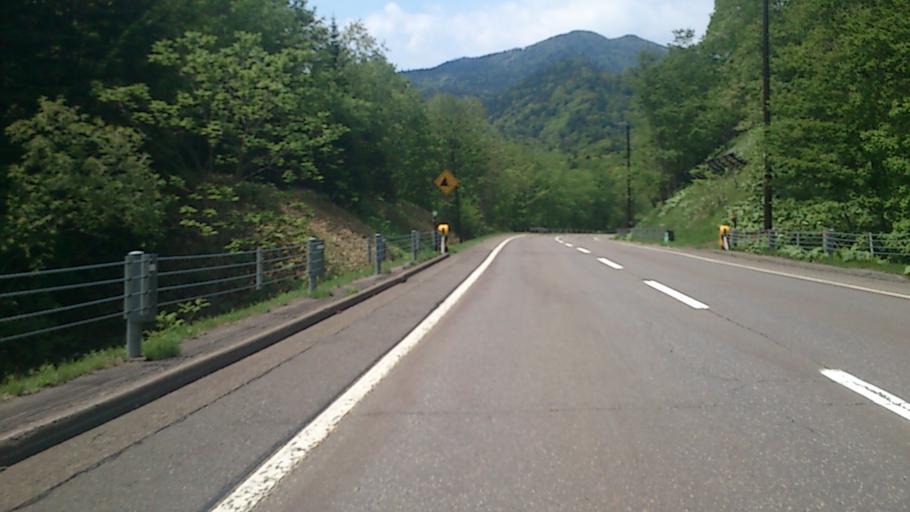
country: JP
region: Hokkaido
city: Otofuke
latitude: 43.3695
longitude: 143.1953
